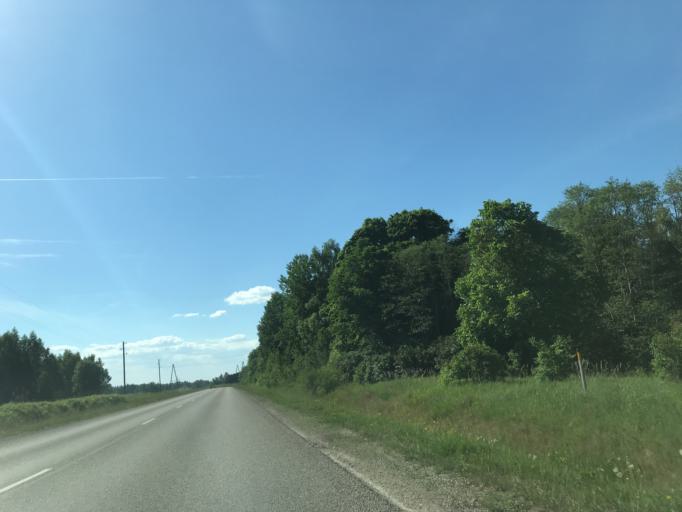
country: LV
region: Aizkraukles Rajons
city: Aizkraukle
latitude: 56.5707
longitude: 25.2447
